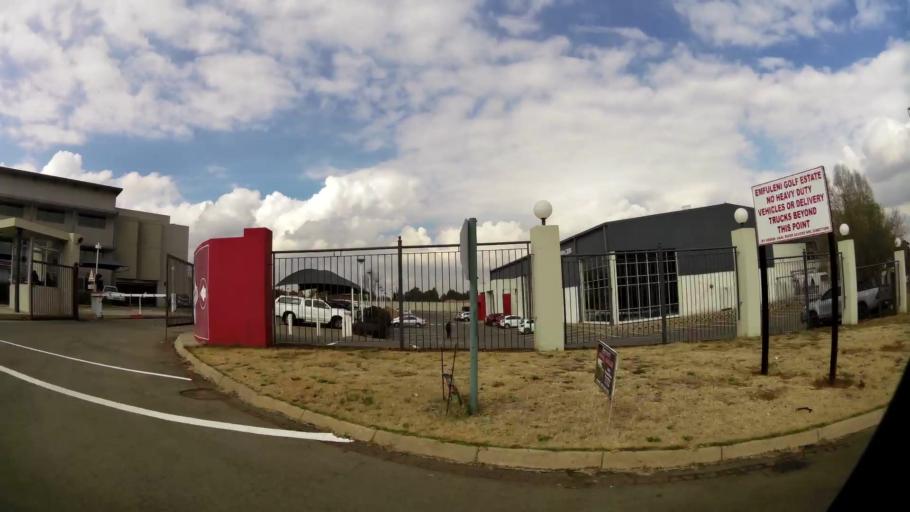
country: ZA
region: Gauteng
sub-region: Sedibeng District Municipality
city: Vanderbijlpark
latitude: -26.7408
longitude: 27.8434
